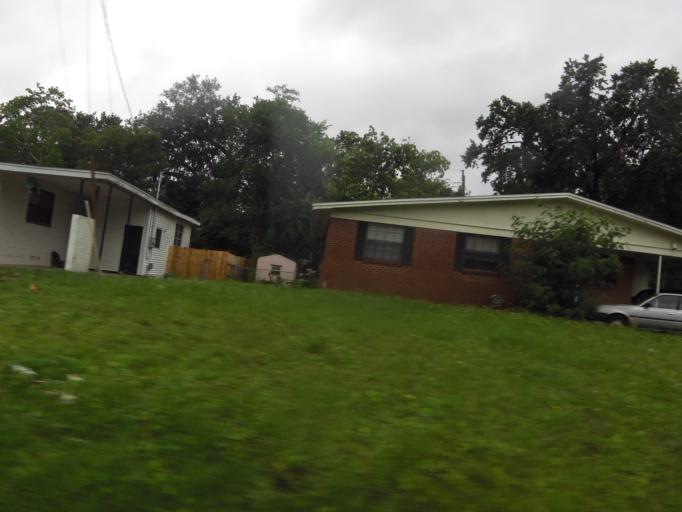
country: US
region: Florida
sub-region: Duval County
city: Jacksonville
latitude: 30.2812
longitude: -81.6261
